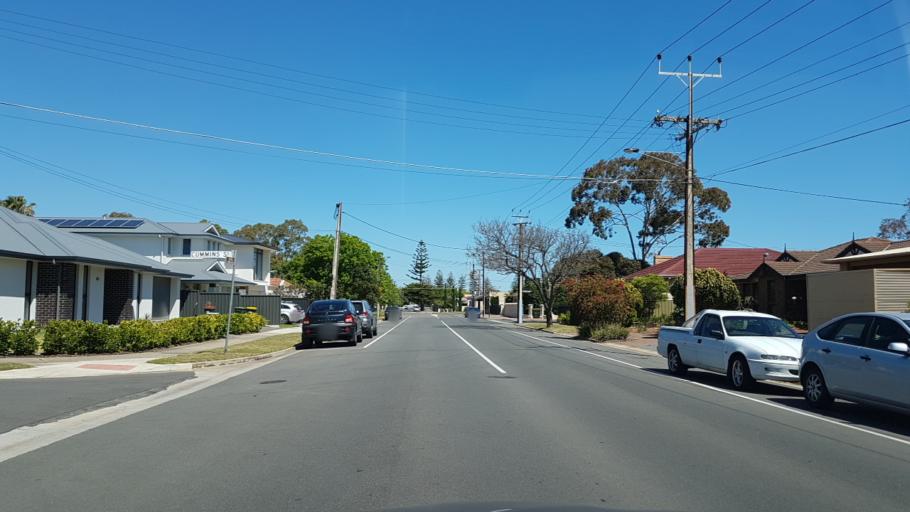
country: AU
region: South Australia
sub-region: Holdfast Bay
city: Glenelg East
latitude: -34.9729
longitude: 138.5285
